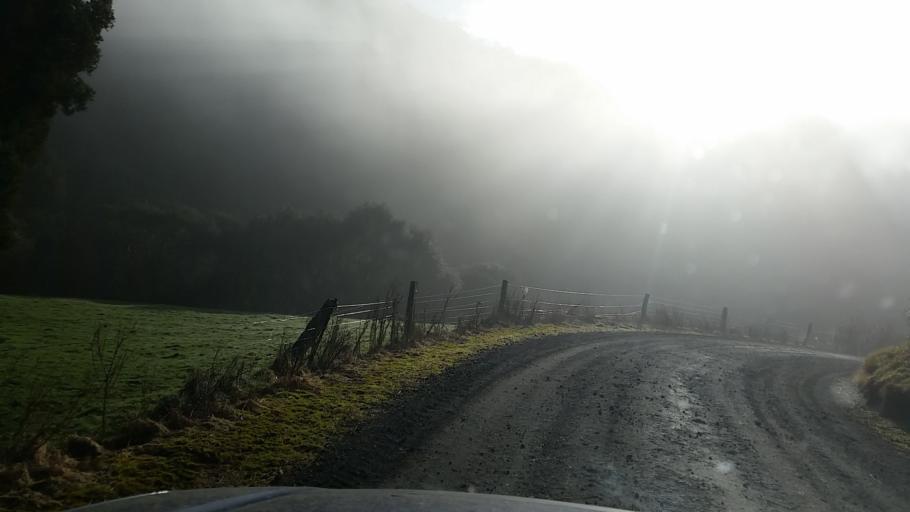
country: NZ
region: Taranaki
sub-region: South Taranaki District
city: Eltham
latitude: -39.3282
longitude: 174.6222
